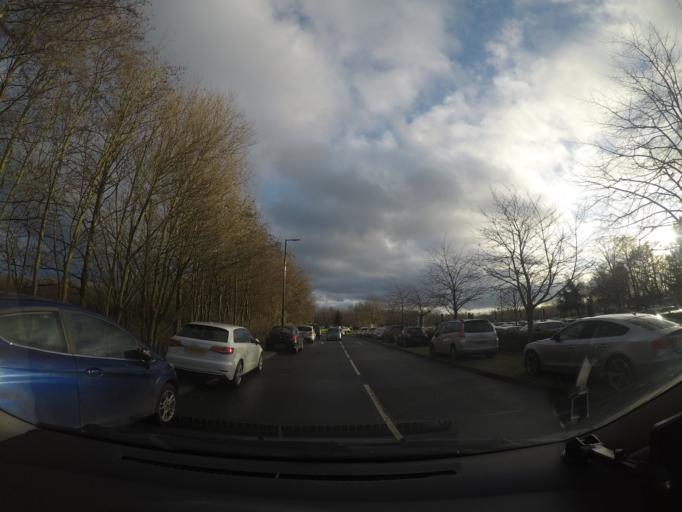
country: GB
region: England
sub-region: City of York
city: Fulford
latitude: 53.9235
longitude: -1.0750
